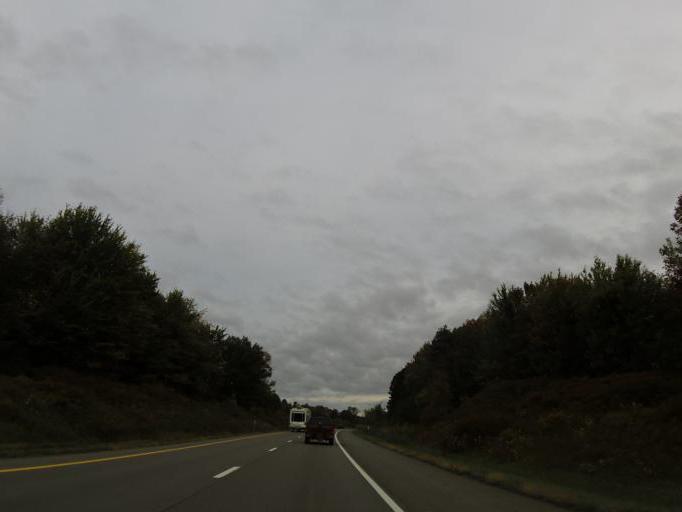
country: US
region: New York
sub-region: Erie County
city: Elma Center
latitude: 42.8165
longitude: -78.6584
